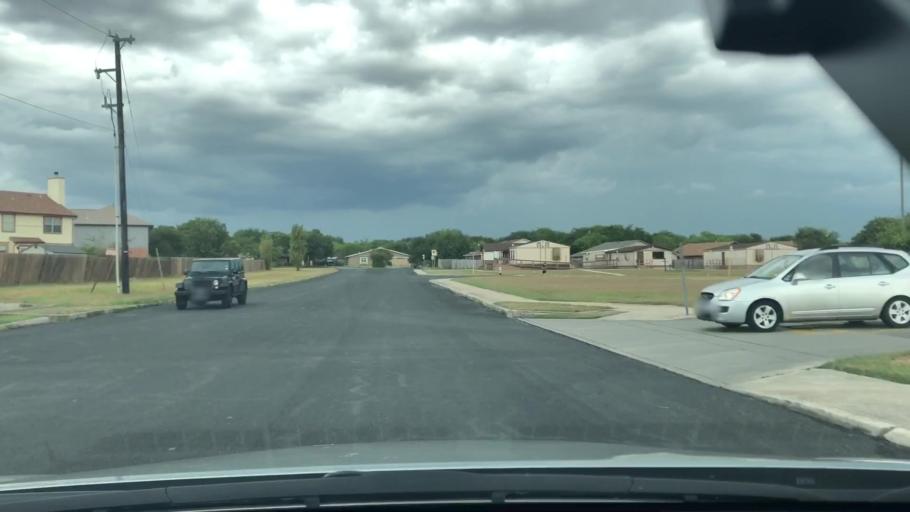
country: US
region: Texas
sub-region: Bexar County
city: Kirby
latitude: 29.4806
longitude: -98.3578
